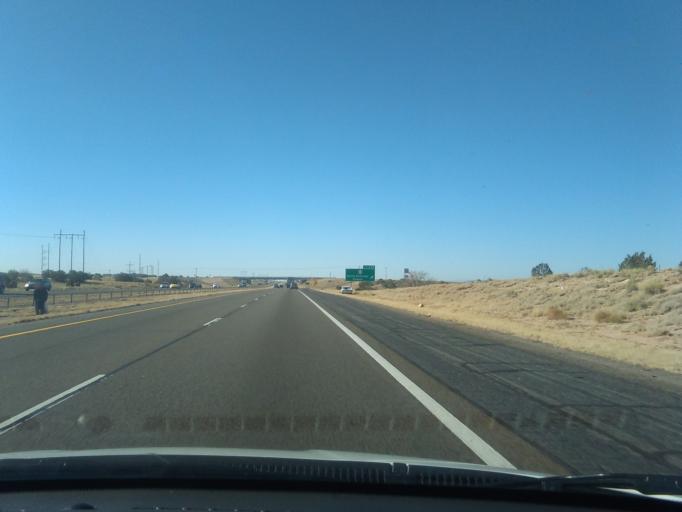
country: US
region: New Mexico
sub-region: Sandoval County
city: Santo Domingo Pueblo
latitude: 35.4734
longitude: -106.2974
